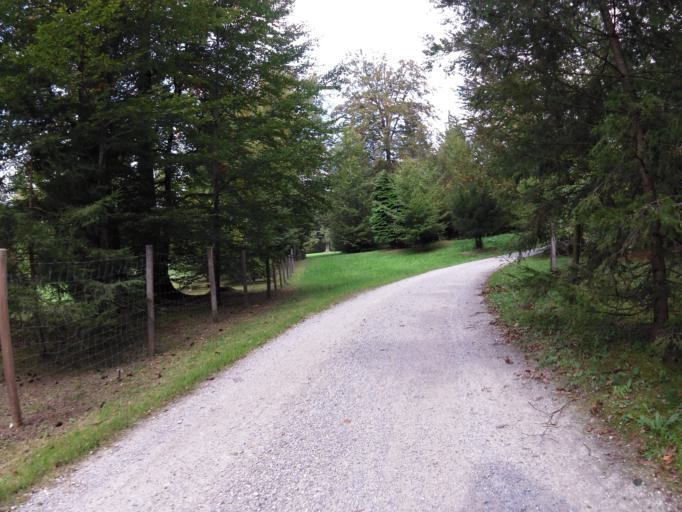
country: DE
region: Bavaria
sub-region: Upper Bavaria
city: Seeshaupt
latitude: 47.8409
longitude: 11.2866
